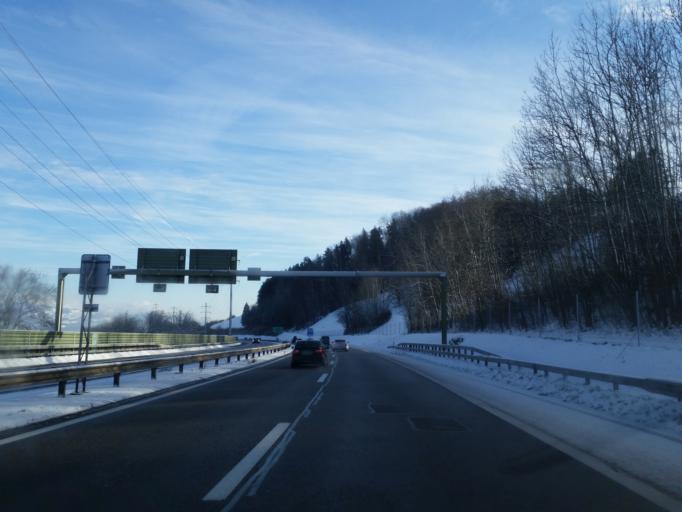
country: CH
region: Schwyz
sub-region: Bezirk Hoefe
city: Wollerau
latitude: 47.1914
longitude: 8.7315
